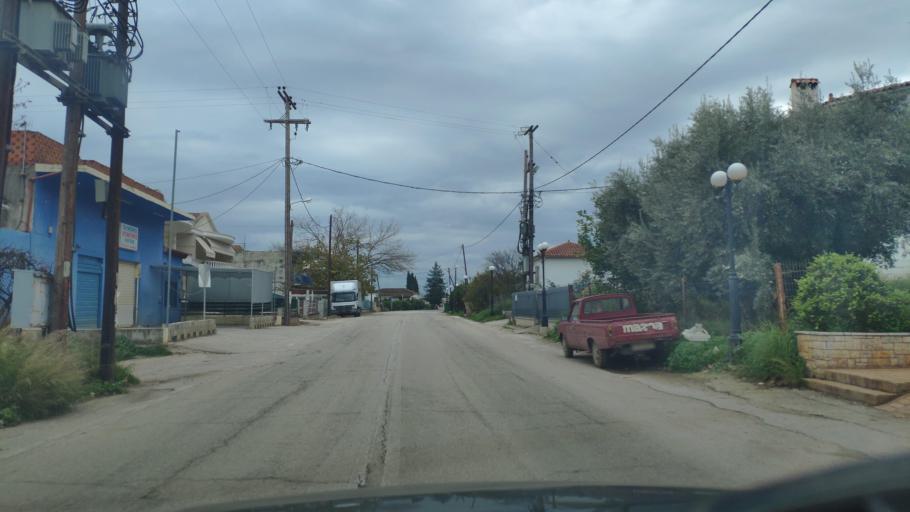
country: GR
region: Peloponnese
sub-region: Nomos Argolidos
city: Nea Kios
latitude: 37.5574
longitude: 22.7134
